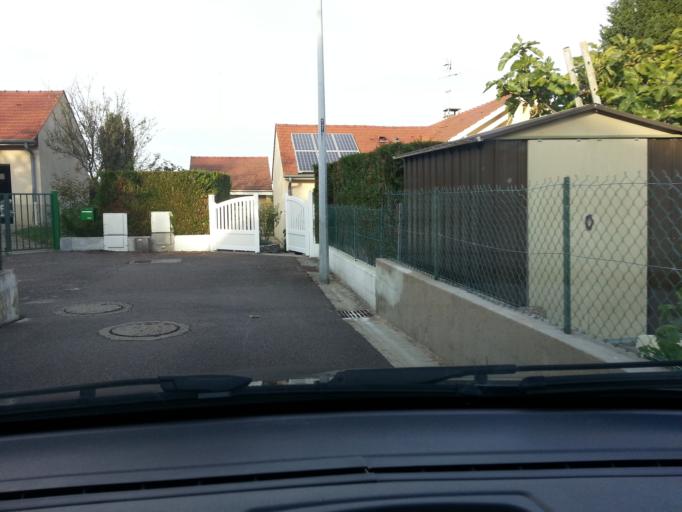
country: FR
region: Bourgogne
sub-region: Departement de Saone-et-Loire
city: Chatenoy-le-Royal
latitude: 46.7821
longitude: 4.8265
